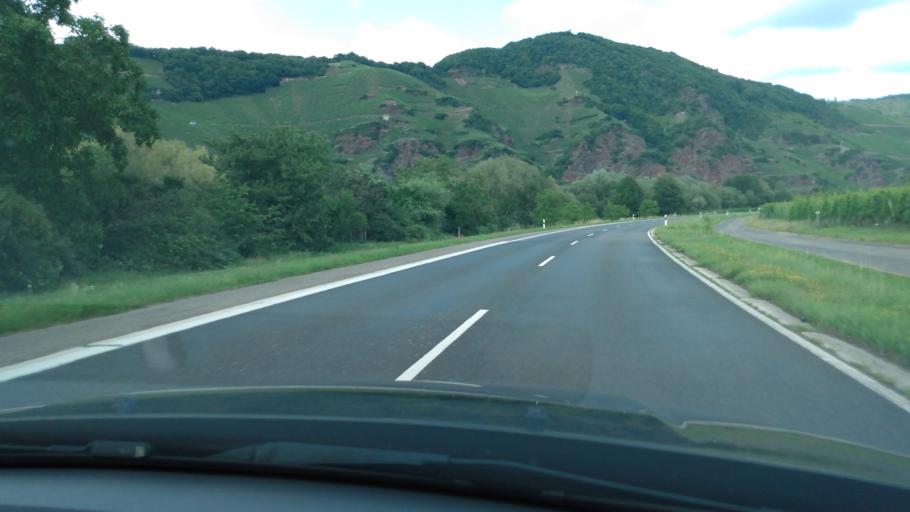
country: DE
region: Rheinland-Pfalz
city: Urzig
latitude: 49.9779
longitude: 7.0108
